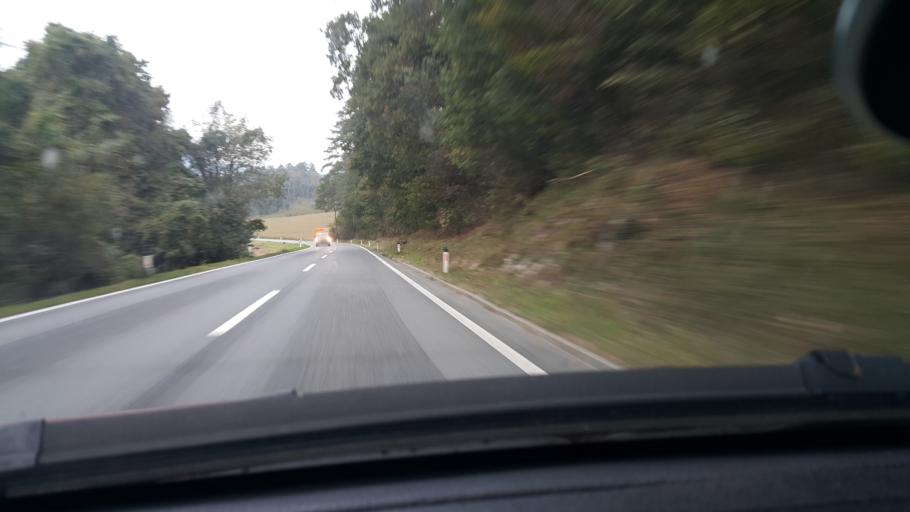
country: AT
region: Carinthia
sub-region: Politischer Bezirk Volkermarkt
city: Neuhaus
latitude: 46.6549
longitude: 14.8890
